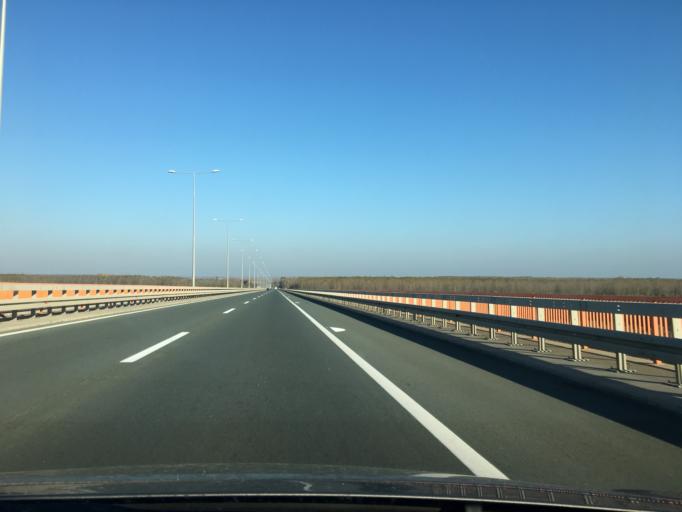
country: RS
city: Beska
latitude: 45.1747
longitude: 20.0791
